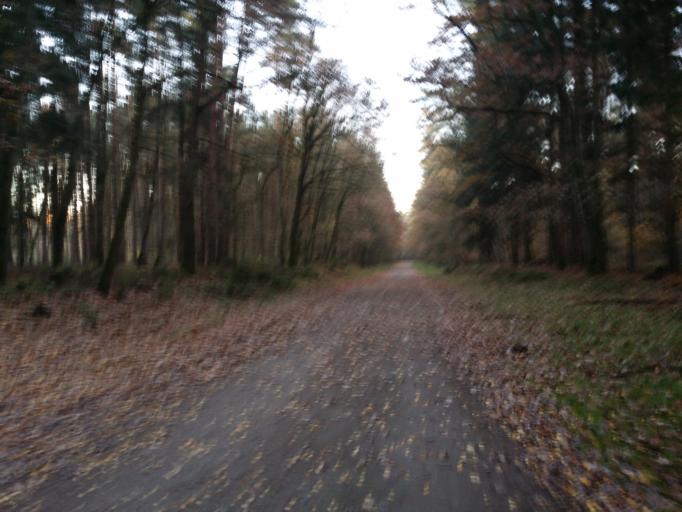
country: DE
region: Lower Saxony
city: Ahausen
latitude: 53.0740
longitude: 9.2868
